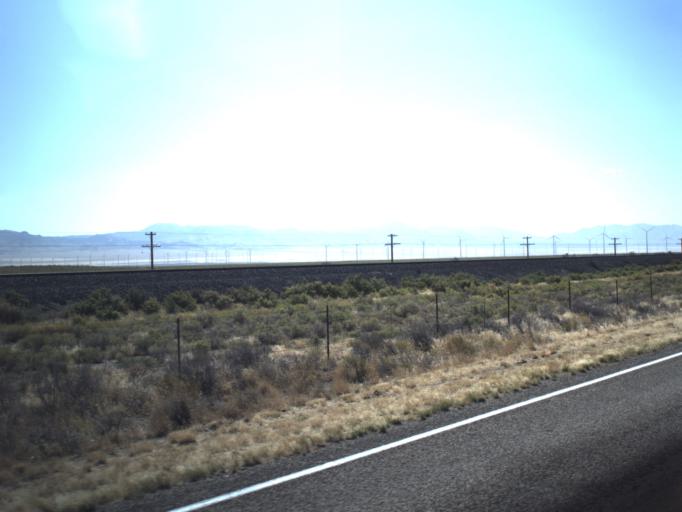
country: US
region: Utah
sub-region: Beaver County
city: Milford
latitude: 38.6227
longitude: -112.9850
